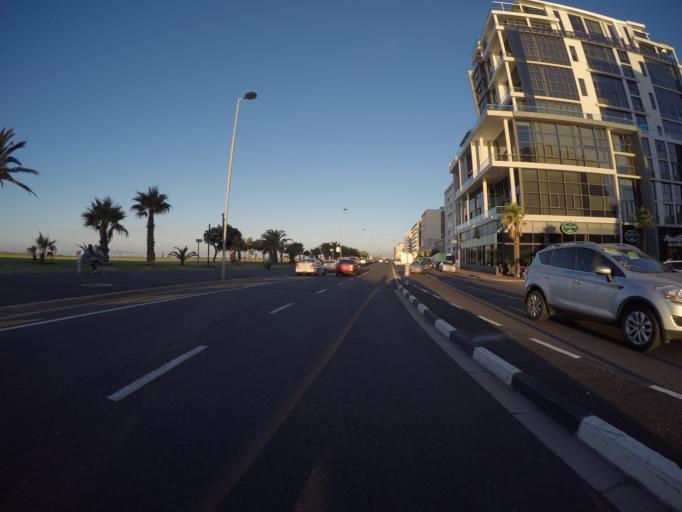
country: ZA
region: Western Cape
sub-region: City of Cape Town
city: Cape Town
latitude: -33.9021
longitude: 18.3994
